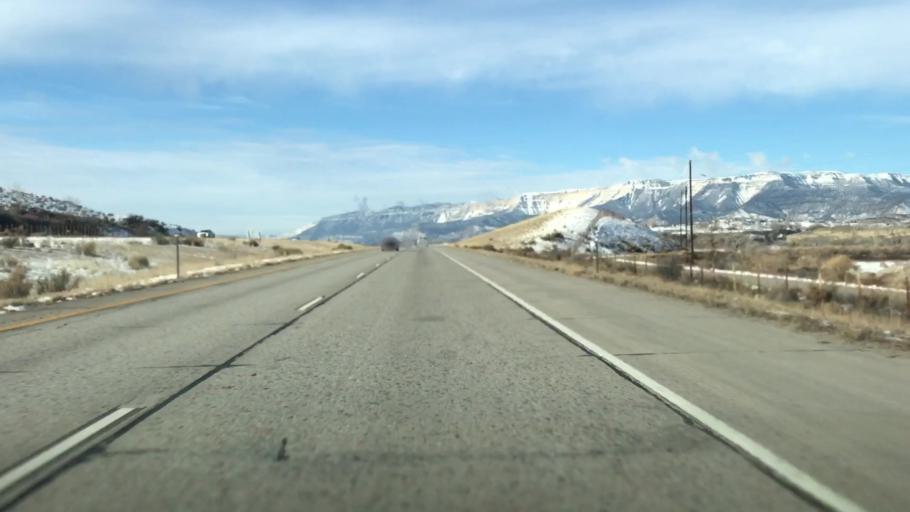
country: US
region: Colorado
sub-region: Garfield County
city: Rifle
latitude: 39.5307
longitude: -107.7325
